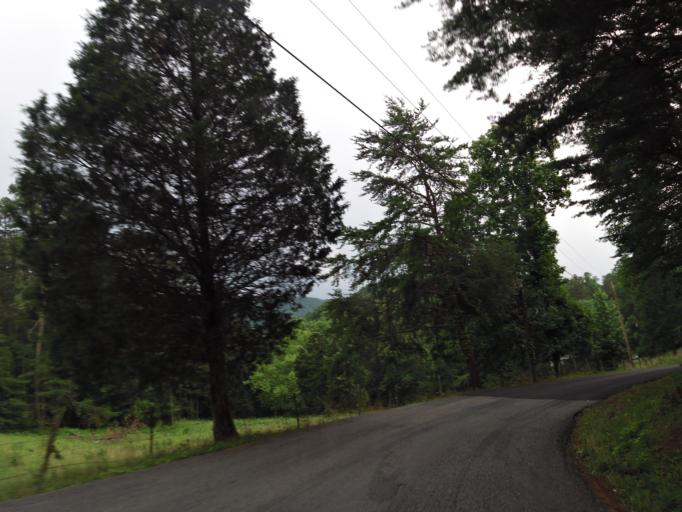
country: US
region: Tennessee
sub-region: Blount County
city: Wildwood
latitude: 35.7447
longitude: -83.7936
